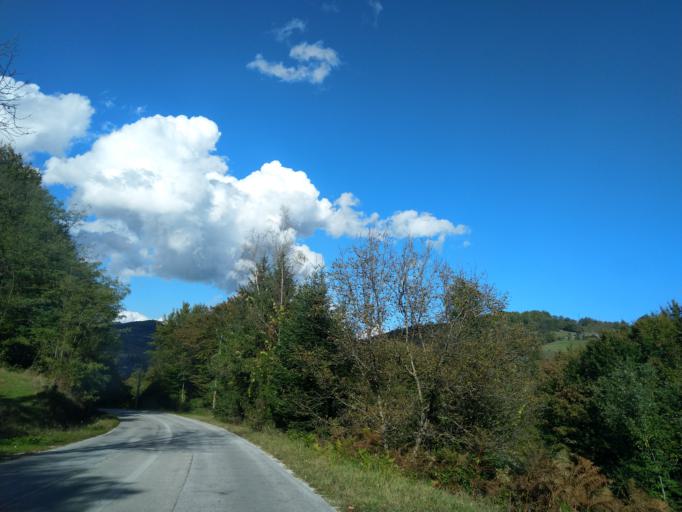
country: RS
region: Central Serbia
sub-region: Zlatiborski Okrug
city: Uzice
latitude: 43.8823
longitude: 19.7751
